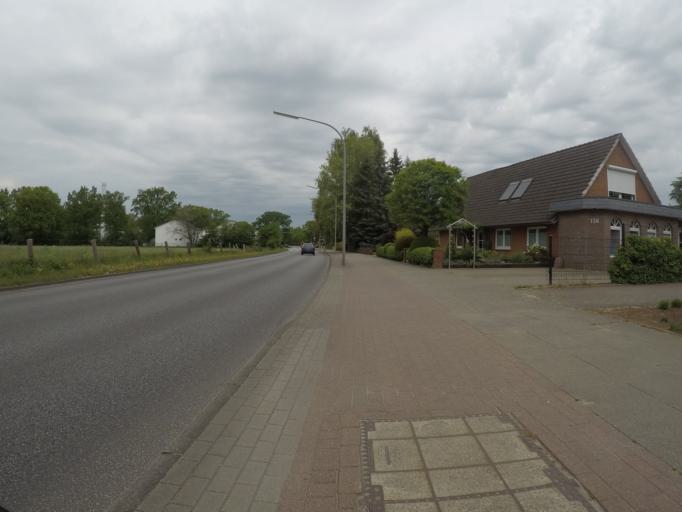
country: DE
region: Schleswig-Holstein
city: Norderstedt
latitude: 53.6889
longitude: 9.9780
